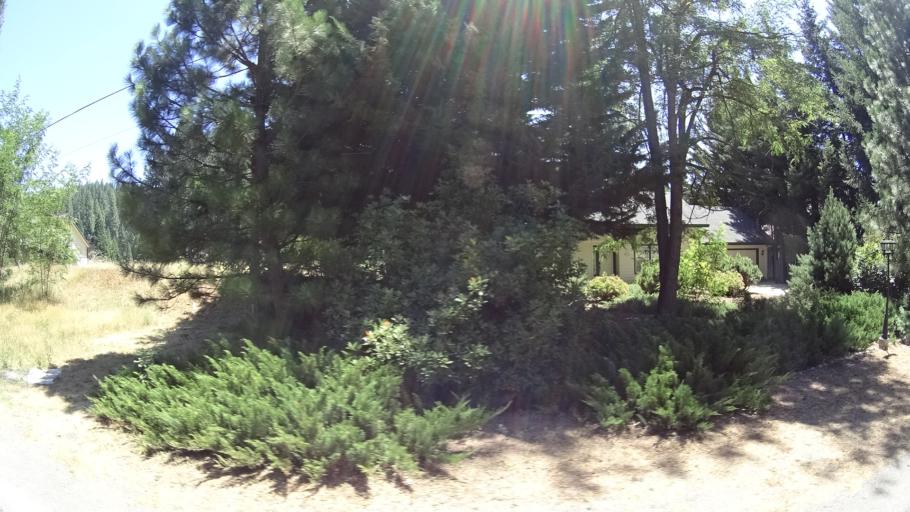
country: US
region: California
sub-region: Calaveras County
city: Arnold
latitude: 38.2511
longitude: -120.3331
